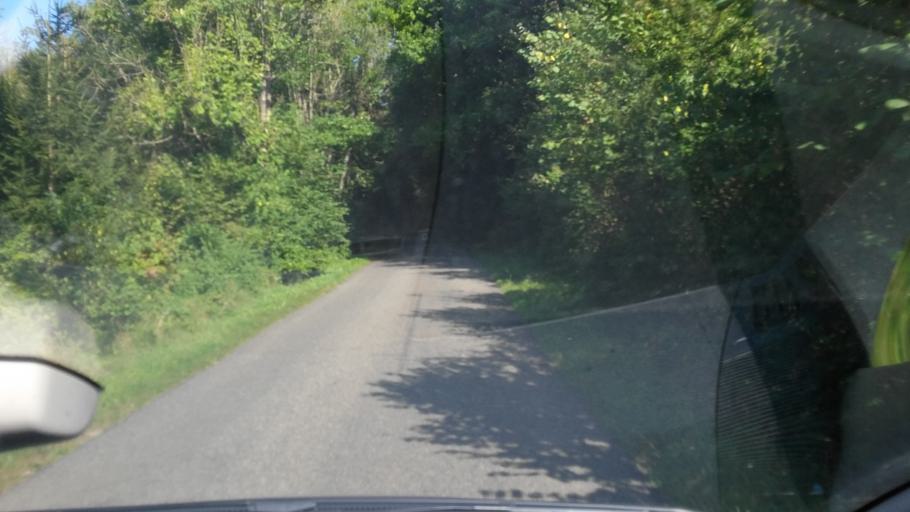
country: BE
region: Wallonia
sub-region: Province du Luxembourg
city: Arlon
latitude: 49.7115
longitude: 5.8384
